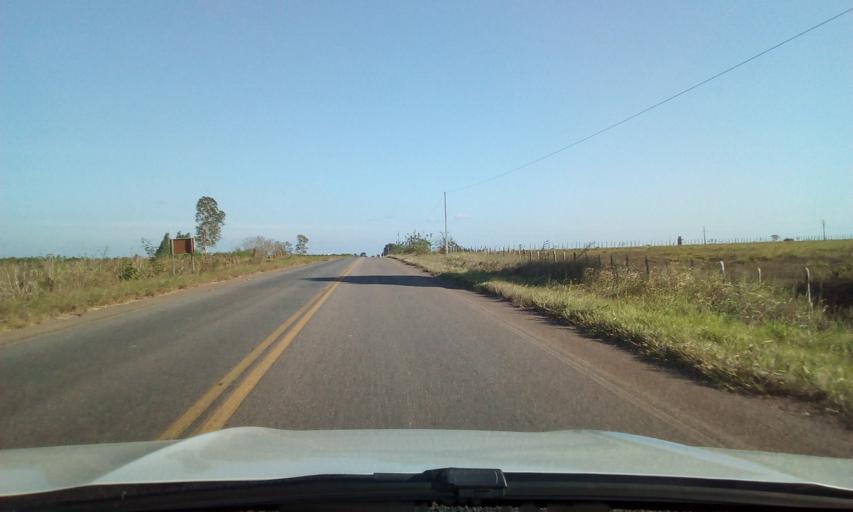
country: BR
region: Paraiba
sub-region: Mari
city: Mari
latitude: -7.0219
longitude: -35.3472
